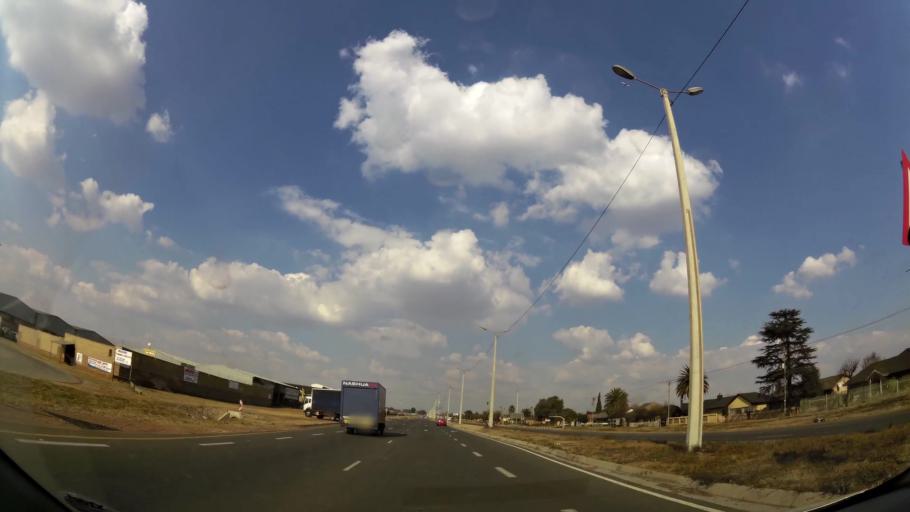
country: ZA
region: Gauteng
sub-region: Ekurhuleni Metropolitan Municipality
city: Germiston
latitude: -26.3071
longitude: 28.1964
